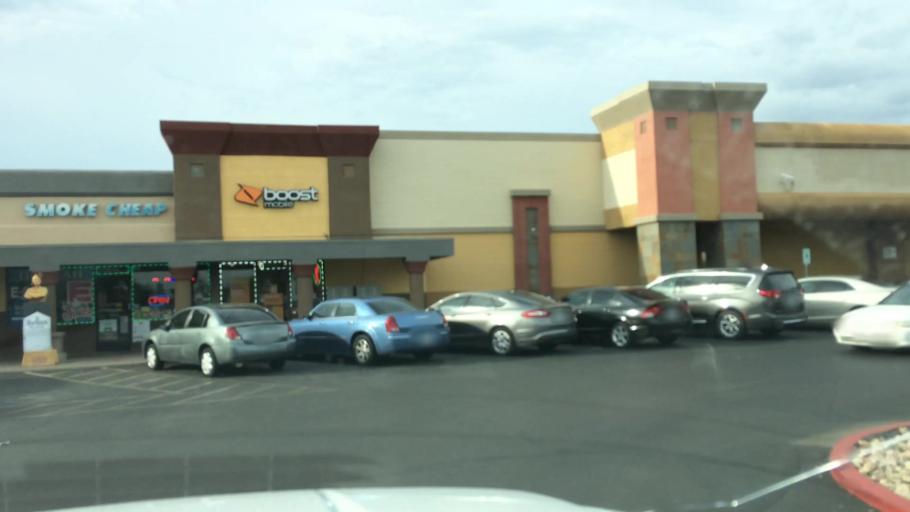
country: US
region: Arizona
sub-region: Maricopa County
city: Glendale
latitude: 33.5685
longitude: -112.1706
